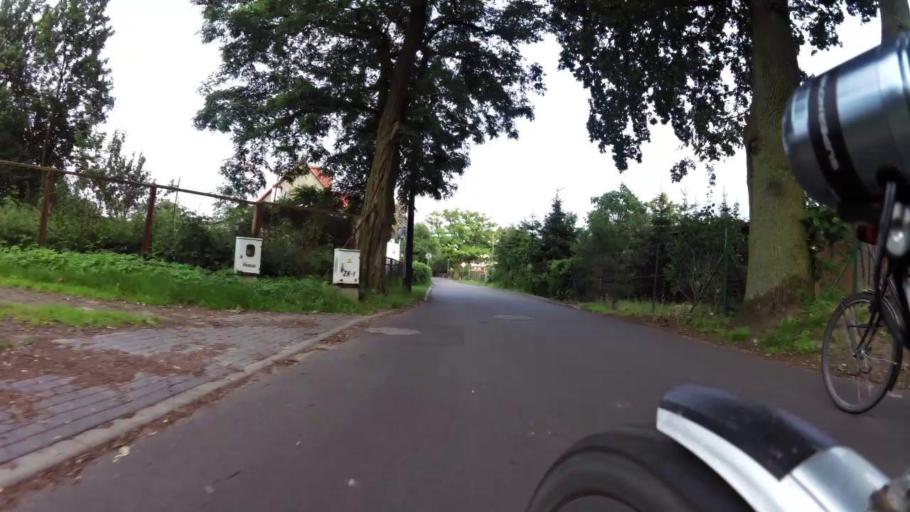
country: PL
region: West Pomeranian Voivodeship
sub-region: Powiat goleniowski
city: Stepnica
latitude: 53.6630
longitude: 14.4963
